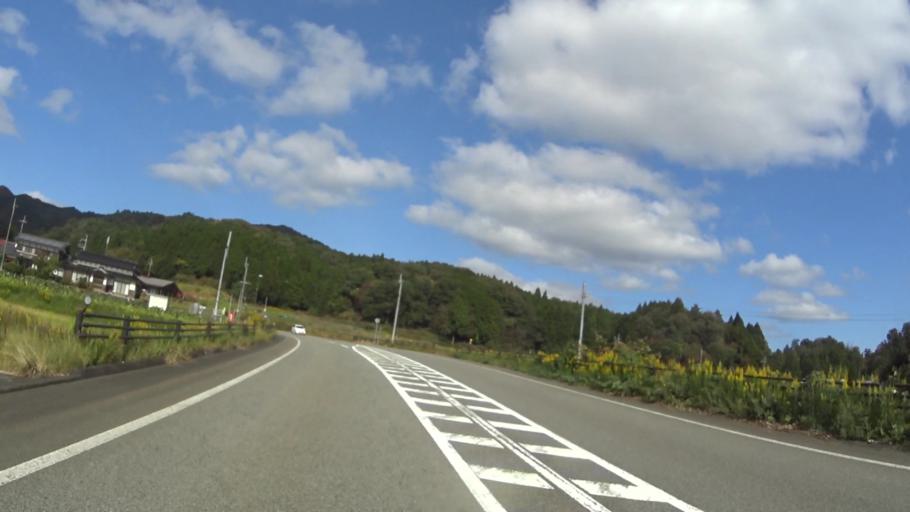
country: JP
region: Hyogo
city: Toyooka
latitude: 35.5082
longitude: 134.9920
